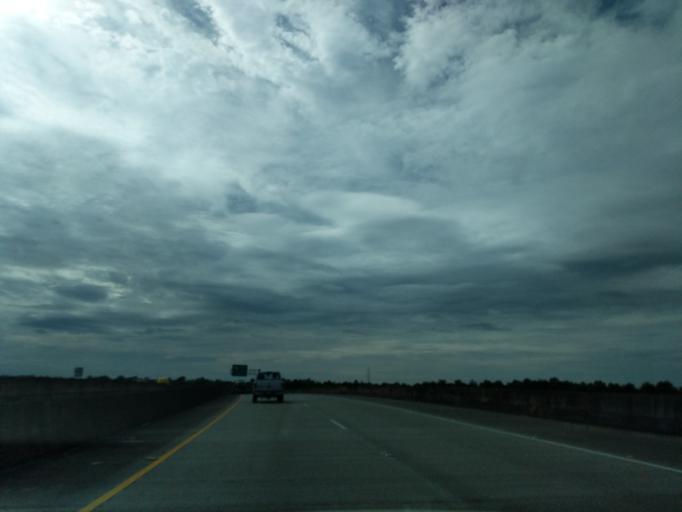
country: US
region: Louisiana
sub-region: Saint Bernard Parish
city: Chalmette
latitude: 30.0179
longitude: -89.9388
